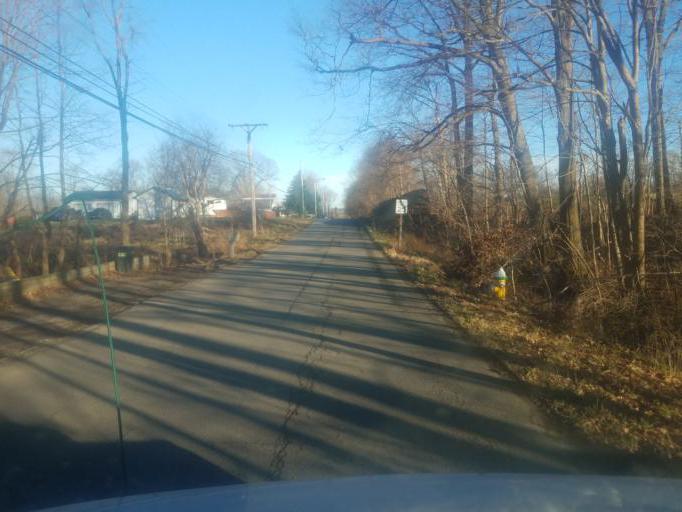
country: US
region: Ohio
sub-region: Richland County
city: Mansfield
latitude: 40.7876
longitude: -82.5375
